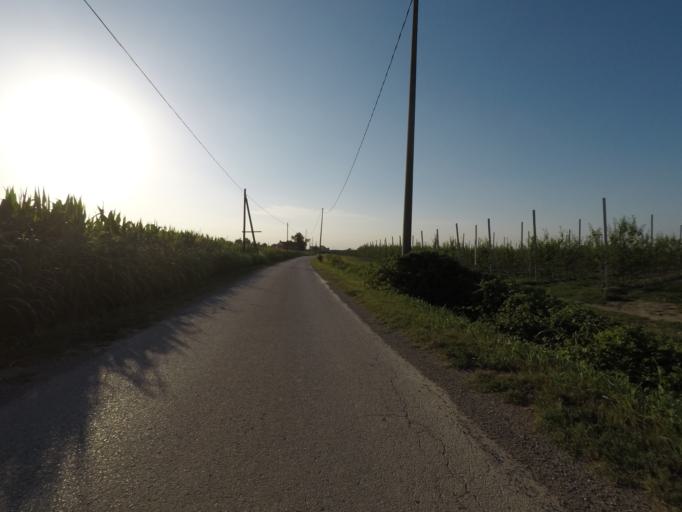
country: IT
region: Veneto
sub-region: Provincia di Rovigo
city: Villamarzana
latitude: 45.0345
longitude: 11.6716
